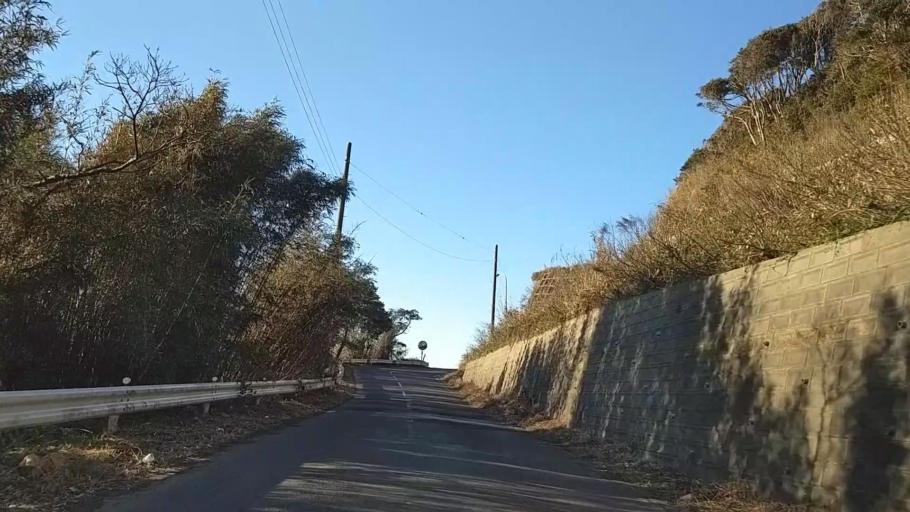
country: JP
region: Chiba
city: Asahi
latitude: 35.7070
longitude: 140.7284
